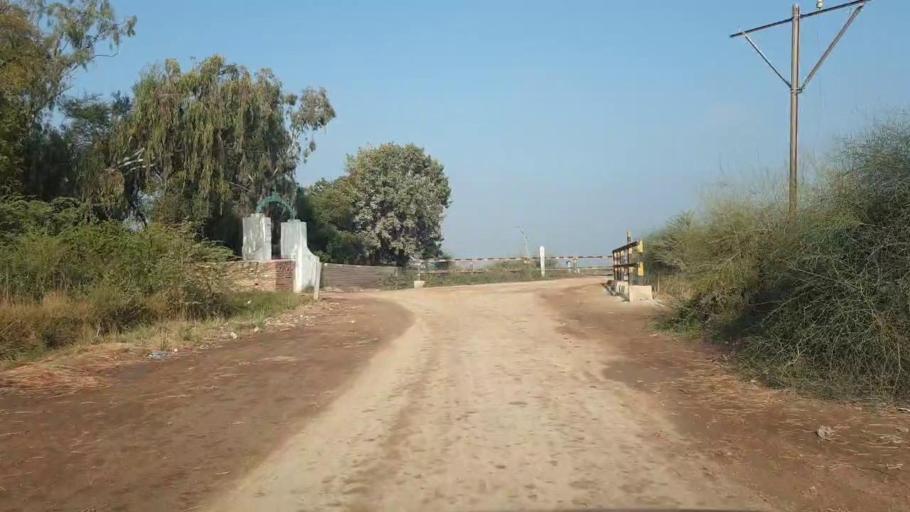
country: PK
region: Sindh
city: Shahdadpur
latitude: 25.9712
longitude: 68.6052
